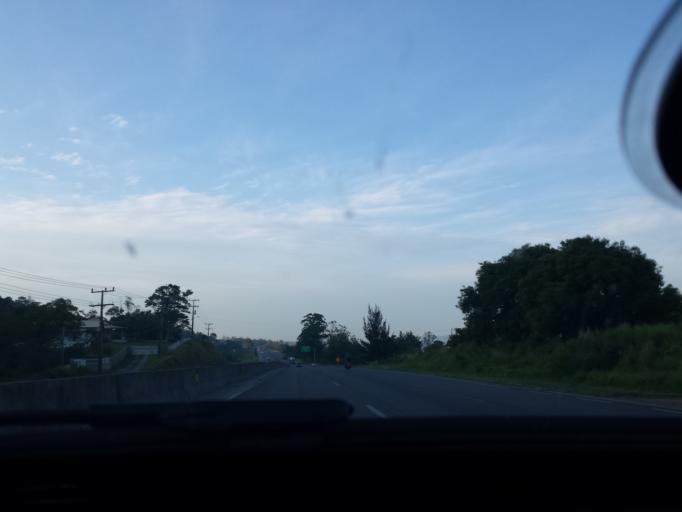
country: BR
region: Santa Catarina
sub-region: Imbituba
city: Imbituba
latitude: -28.2510
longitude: -48.7017
